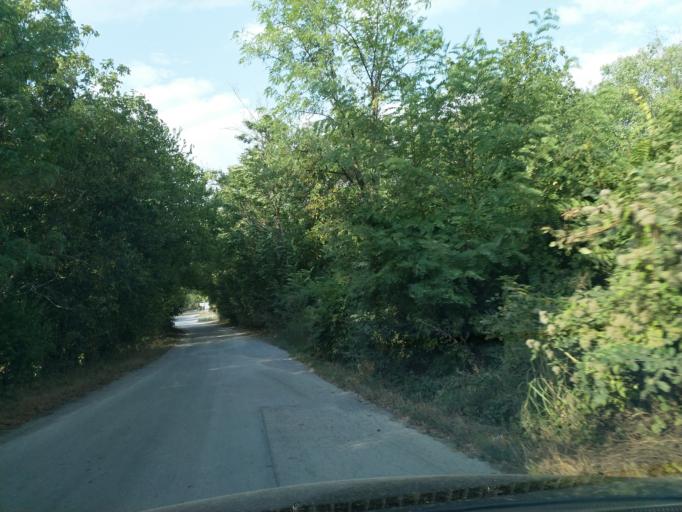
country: RS
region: Central Serbia
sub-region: Pomoravski Okrug
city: Paracin
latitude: 43.8467
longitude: 21.5274
